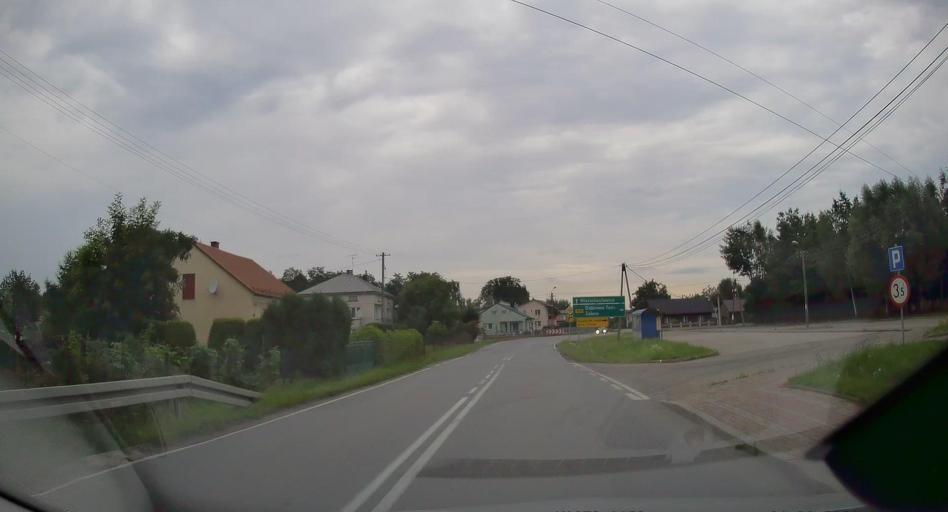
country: PL
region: Lesser Poland Voivodeship
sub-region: Powiat tarnowski
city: Wojnicz
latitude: 49.9928
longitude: 20.8397
